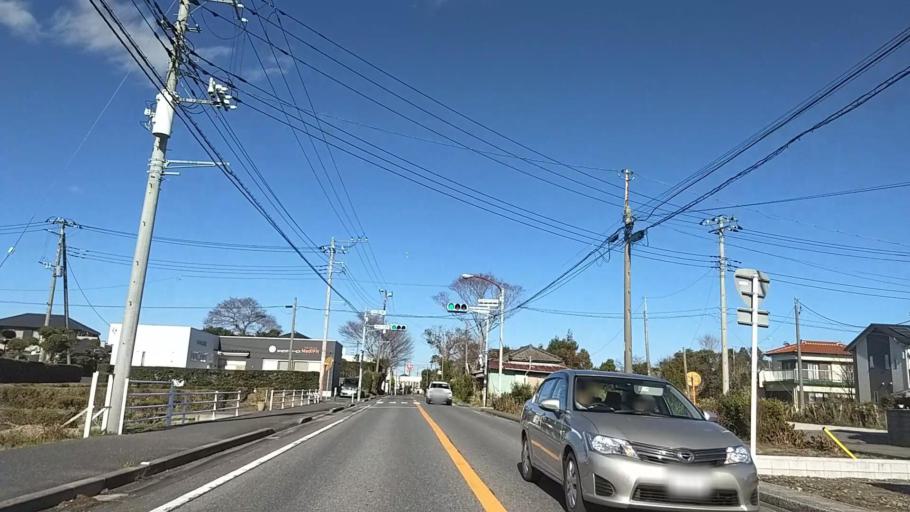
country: JP
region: Chiba
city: Ohara
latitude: 35.2441
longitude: 140.3933
